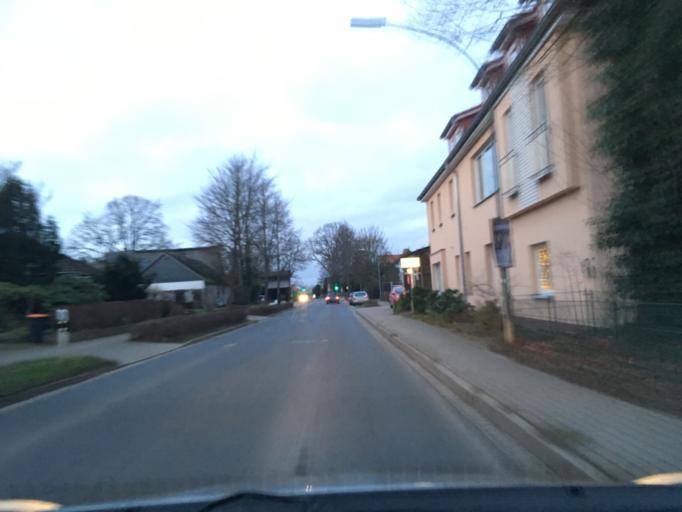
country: DE
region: Lower Saxony
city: Wulfsen
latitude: 53.3471
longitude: 10.1475
